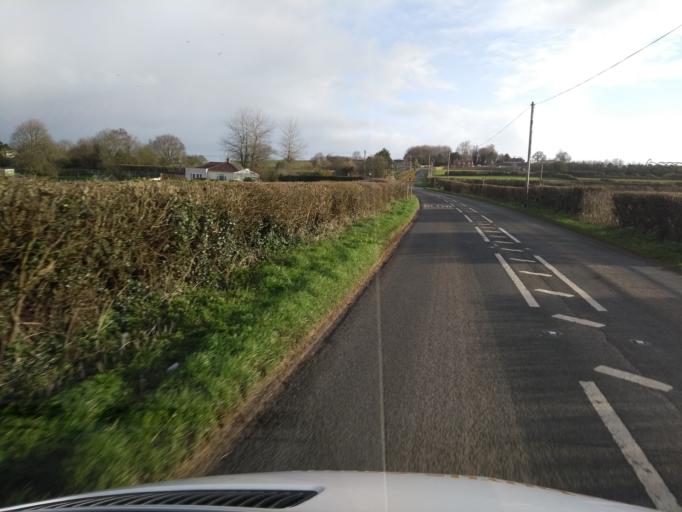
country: GB
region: England
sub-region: Somerset
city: Castle Cary
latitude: 51.0726
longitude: -2.5165
